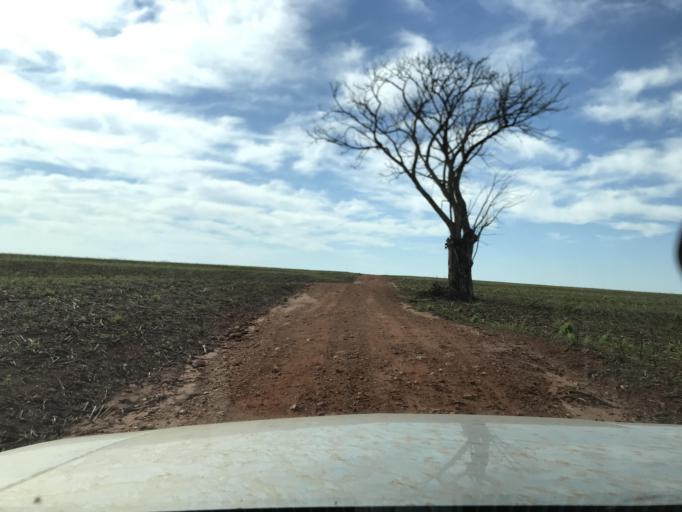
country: BR
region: Parana
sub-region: Palotina
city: Palotina
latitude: -24.1886
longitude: -53.8331
